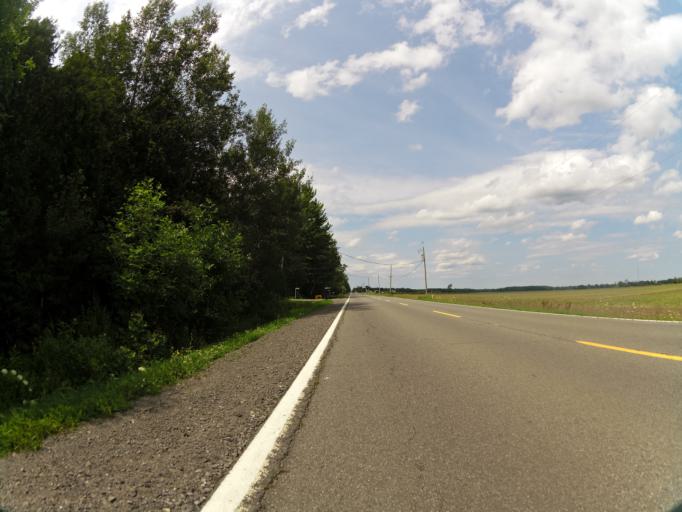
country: CA
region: Ontario
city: Ottawa
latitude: 45.1892
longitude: -75.5852
